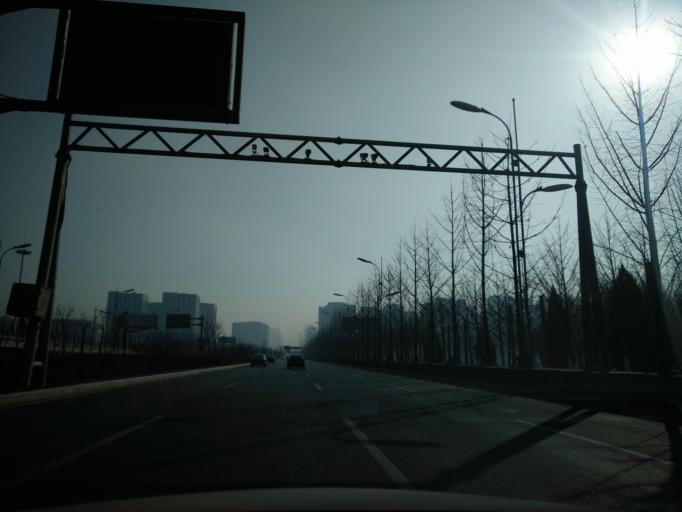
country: CN
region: Beijing
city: Jiugong
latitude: 39.8127
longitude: 116.4867
